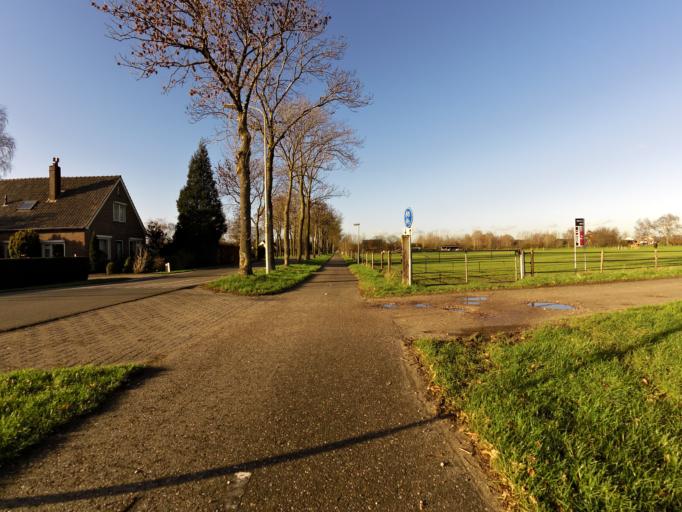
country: NL
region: Gelderland
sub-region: Gemeente Doesburg
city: Doesburg
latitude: 51.9281
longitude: 6.1790
